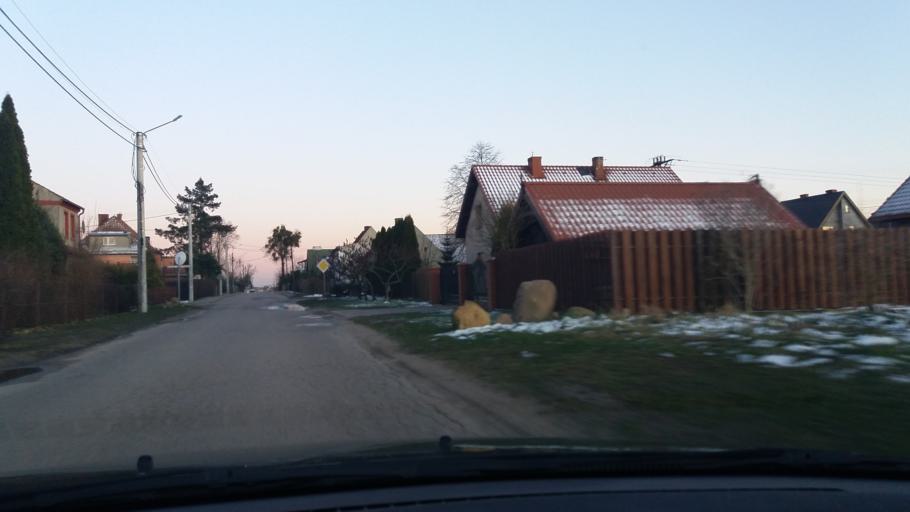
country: PL
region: Warmian-Masurian Voivodeship
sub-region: Powiat szczycienski
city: Szczytno
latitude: 53.5607
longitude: 20.9683
